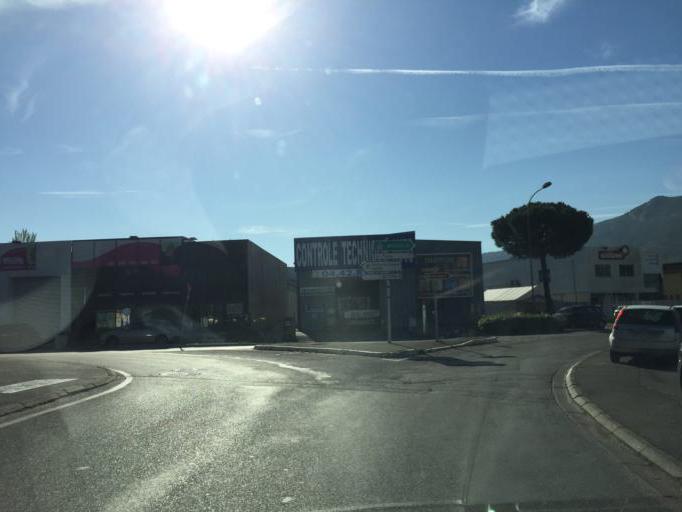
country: FR
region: Provence-Alpes-Cote d'Azur
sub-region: Departement des Bouches-du-Rhone
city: Gemenos
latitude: 43.2881
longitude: 5.6012
